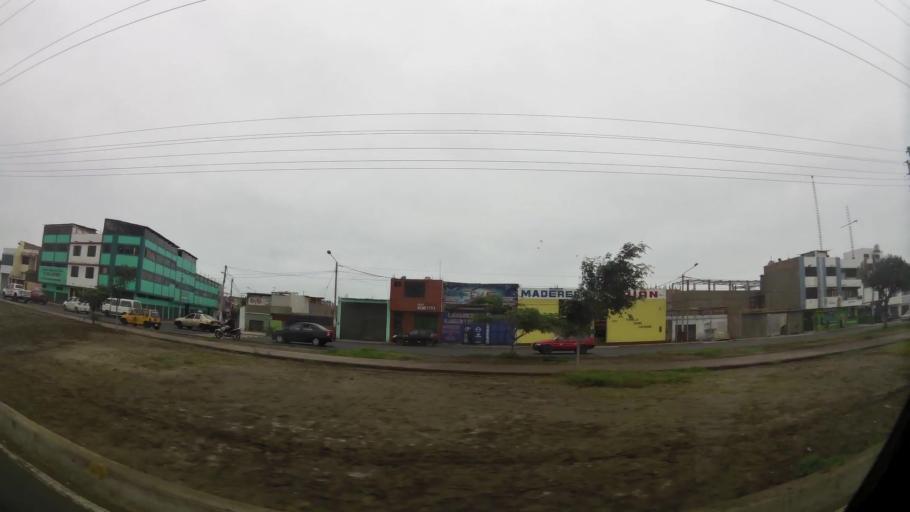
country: PE
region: Ancash
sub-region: Provincia de Santa
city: Chimbote
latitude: -9.0896
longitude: -78.5694
